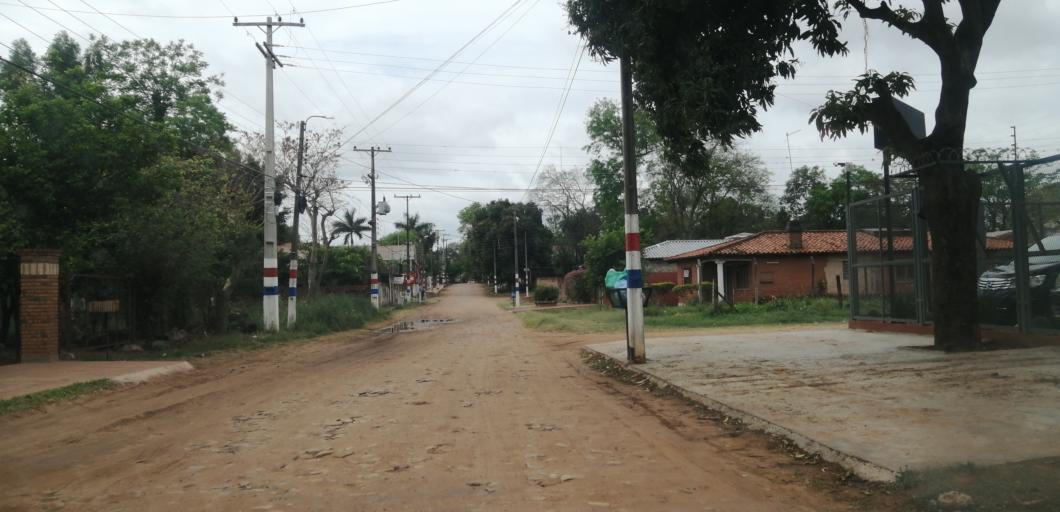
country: PY
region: Central
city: Colonia Mariano Roque Alonso
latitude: -25.1939
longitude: -57.5393
